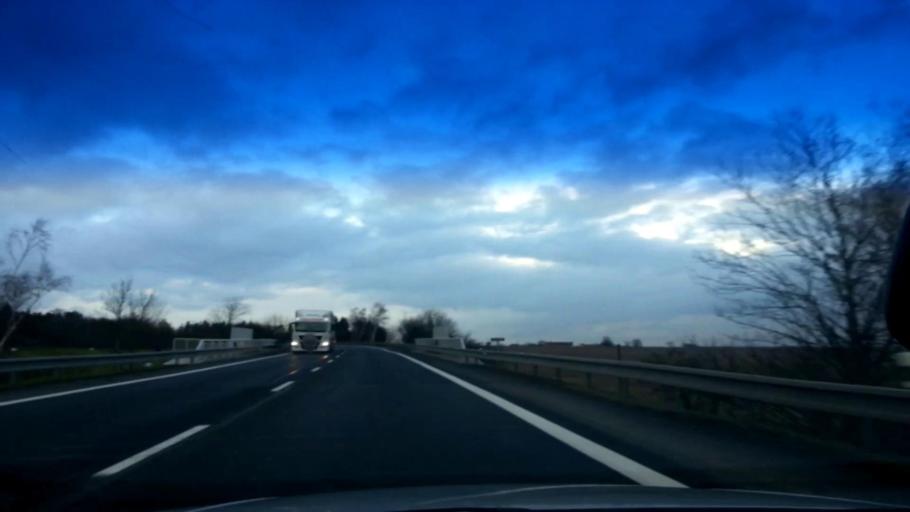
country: CZ
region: Karlovarsky
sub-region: Okres Cheb
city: Frantiskovy Lazne
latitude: 50.1148
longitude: 12.3736
